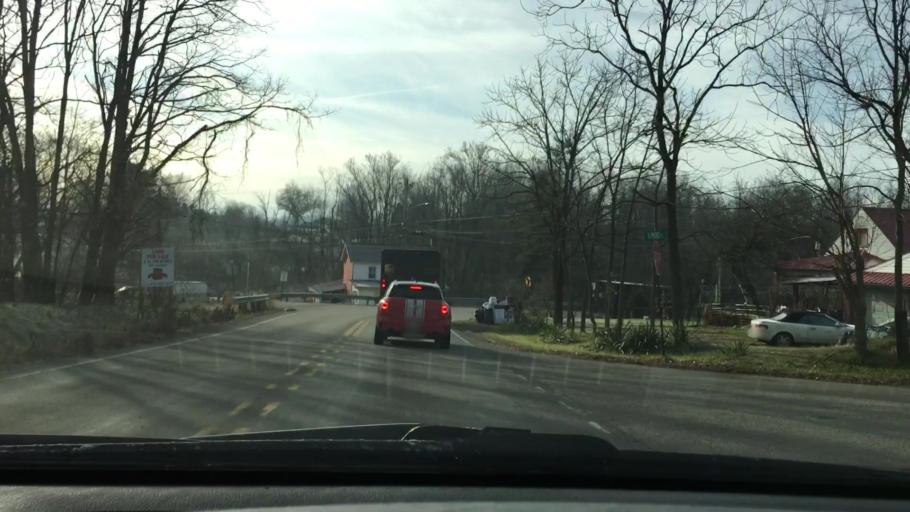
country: US
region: Pennsylvania
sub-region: Allegheny County
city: Industry
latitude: 40.2405
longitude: -79.7938
